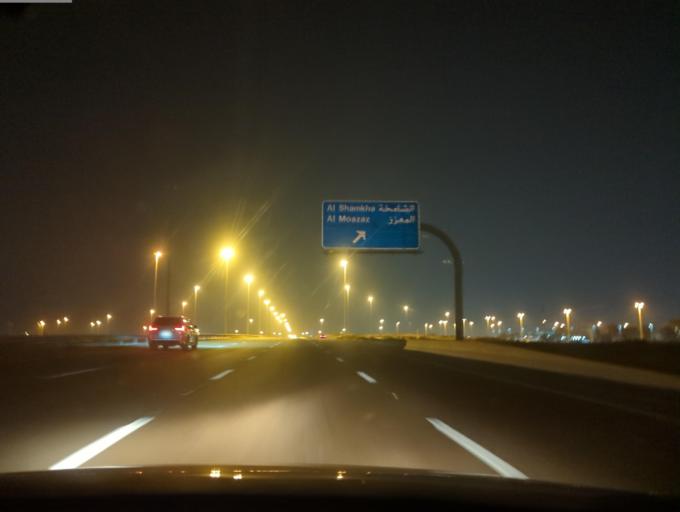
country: AE
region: Abu Dhabi
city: Abu Dhabi
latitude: 24.3841
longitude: 54.7379
